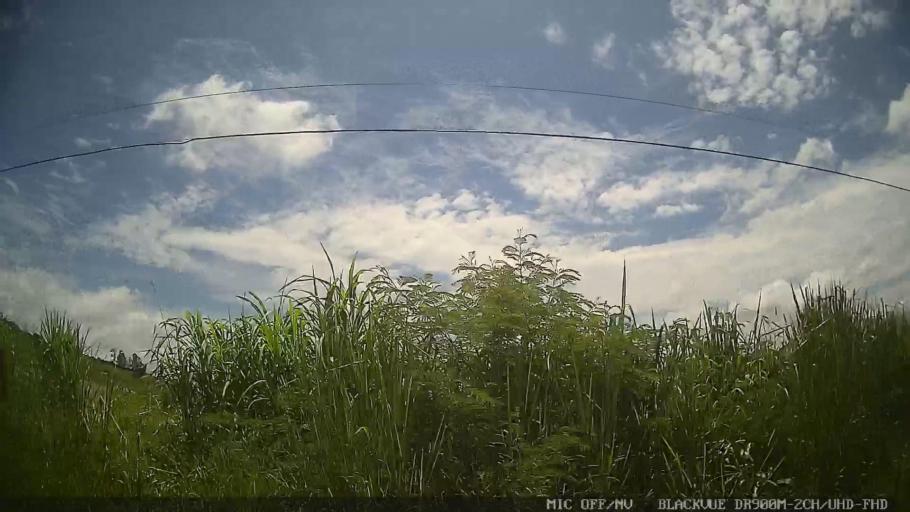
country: BR
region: Sao Paulo
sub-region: Laranjal Paulista
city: Laranjal Paulista
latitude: -23.0217
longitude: -47.8510
